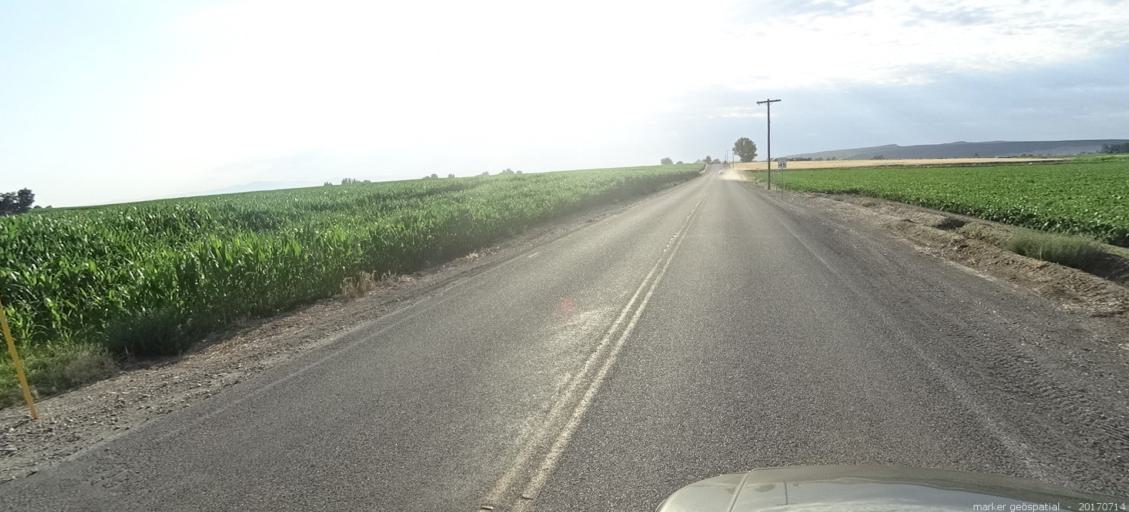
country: US
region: Idaho
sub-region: Canyon County
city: Nampa
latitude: 43.4593
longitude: -116.5135
